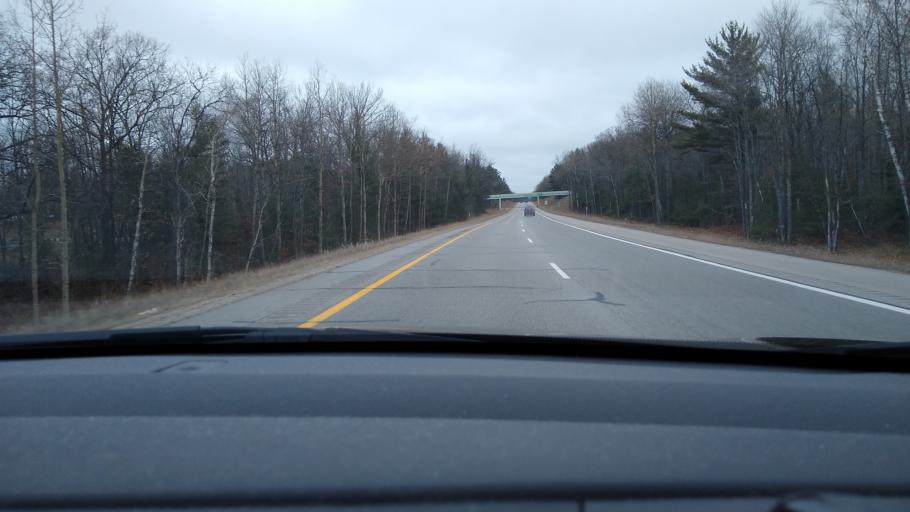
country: US
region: Michigan
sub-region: Otsego County
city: Gaylord
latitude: 44.9128
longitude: -84.6904
